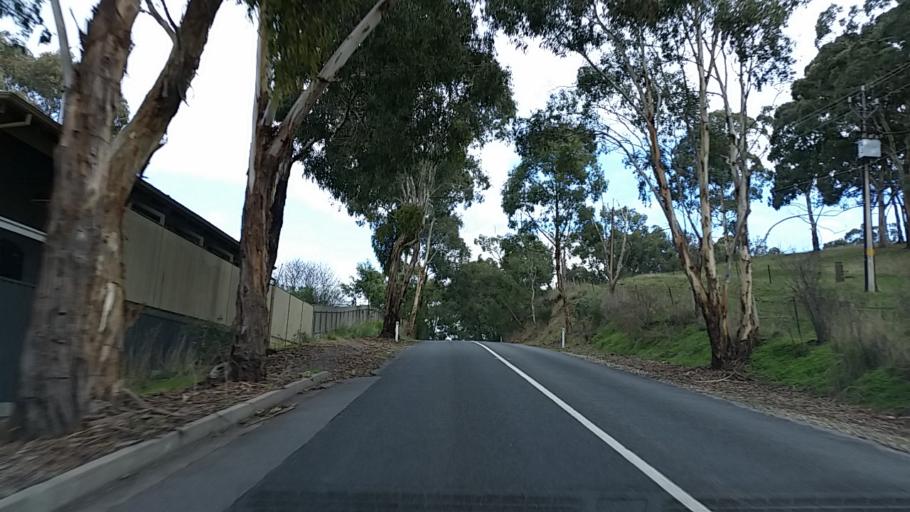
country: AU
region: South Australia
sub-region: Mount Barker
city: Little Hampton
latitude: -35.0689
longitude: 138.8440
